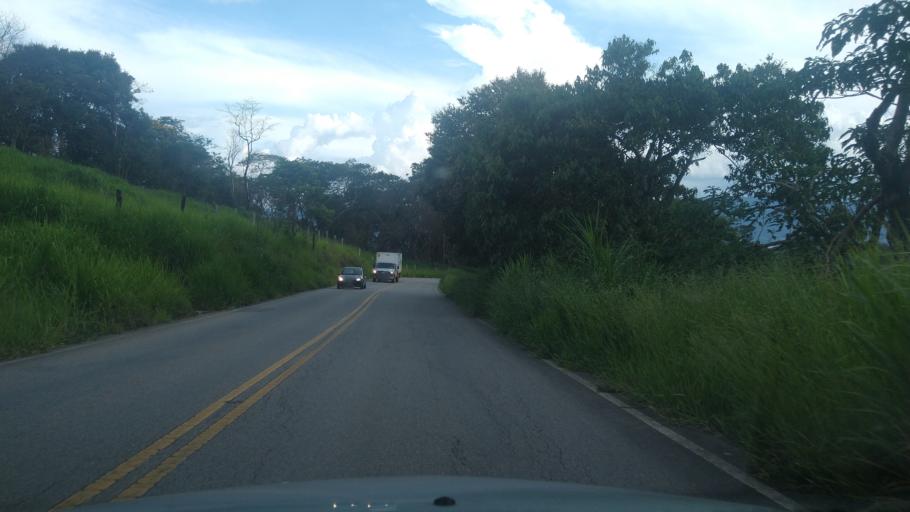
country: BR
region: Minas Gerais
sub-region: Extrema
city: Extrema
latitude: -22.7817
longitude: -46.3214
